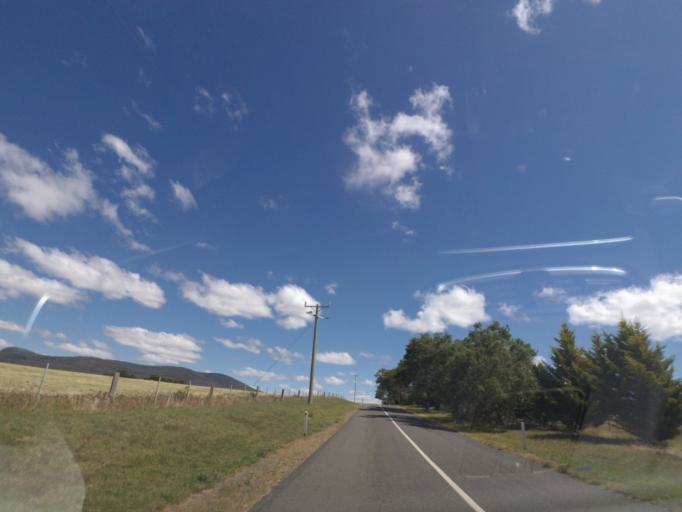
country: AU
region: Victoria
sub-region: Hume
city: Sunbury
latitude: -37.3335
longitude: 144.5585
